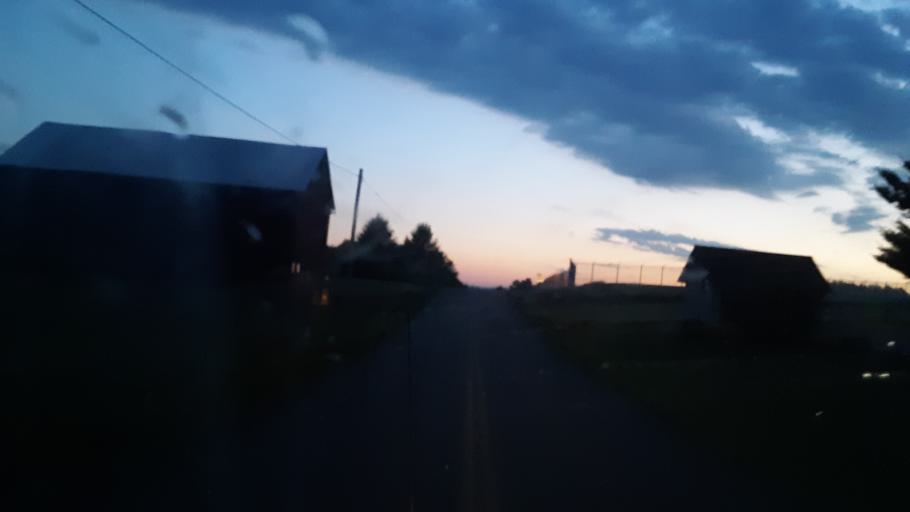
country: US
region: Ohio
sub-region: Carroll County
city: Carrollton
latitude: 40.5573
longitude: -81.0869
